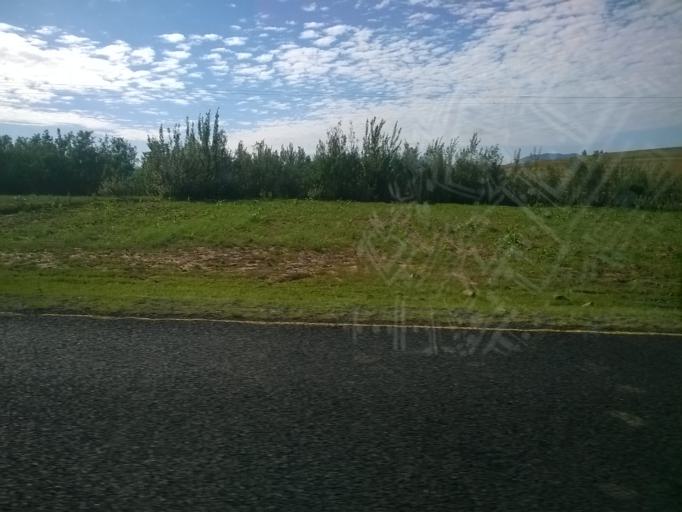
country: LS
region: Berea
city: Teyateyaneng
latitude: -29.1184
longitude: 27.7966
